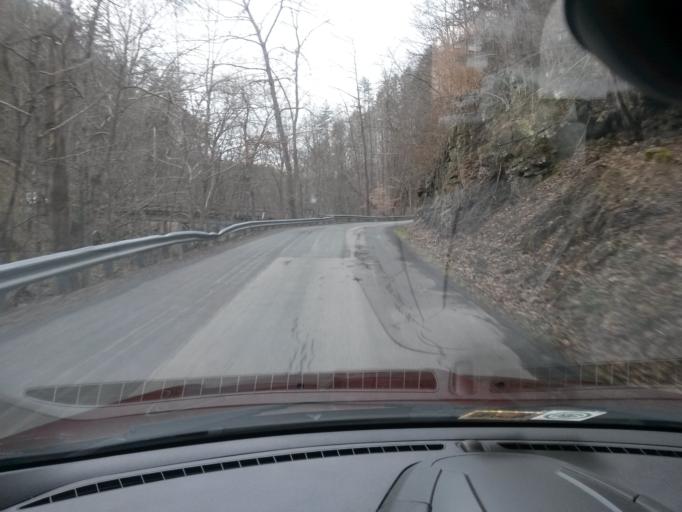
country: US
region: Virginia
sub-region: Bath County
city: Warm Springs
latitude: 38.0405
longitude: -79.8578
